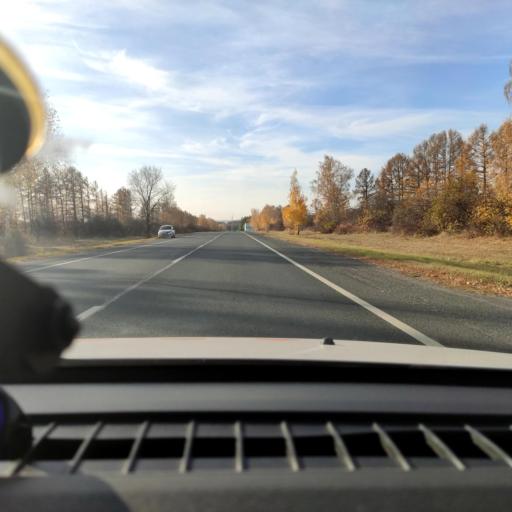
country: RU
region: Samara
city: Volzhskiy
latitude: 53.4602
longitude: 50.1271
